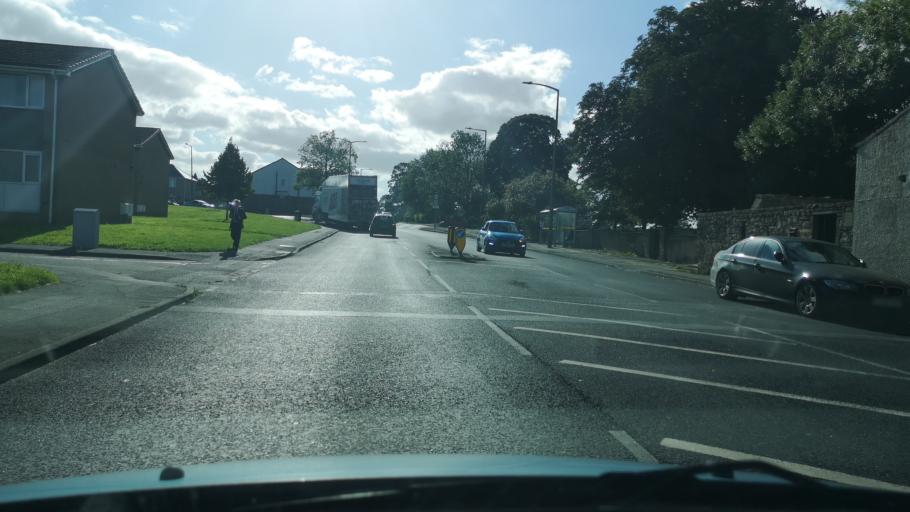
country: GB
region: England
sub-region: Doncaster
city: Carcroft
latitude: 53.5694
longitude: -1.1840
